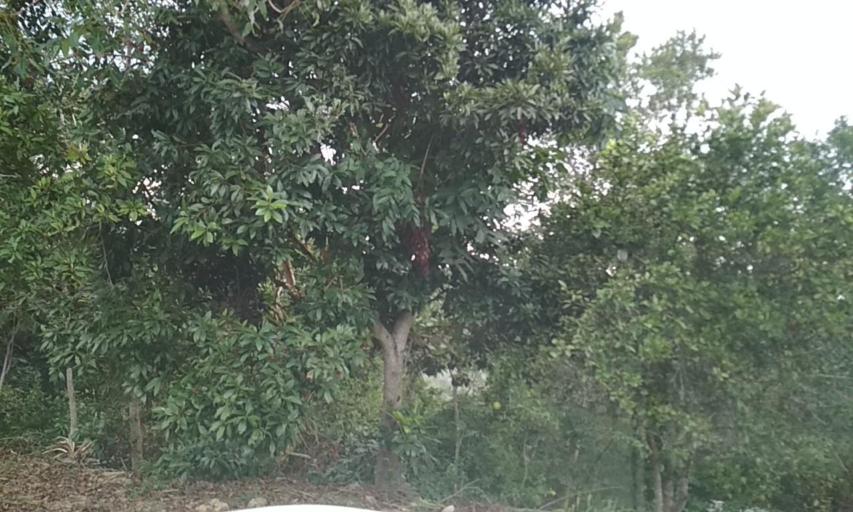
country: MX
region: Veracruz
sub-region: Coatzintla
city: Manuel Maria Contreras
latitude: 20.3794
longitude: -97.4441
